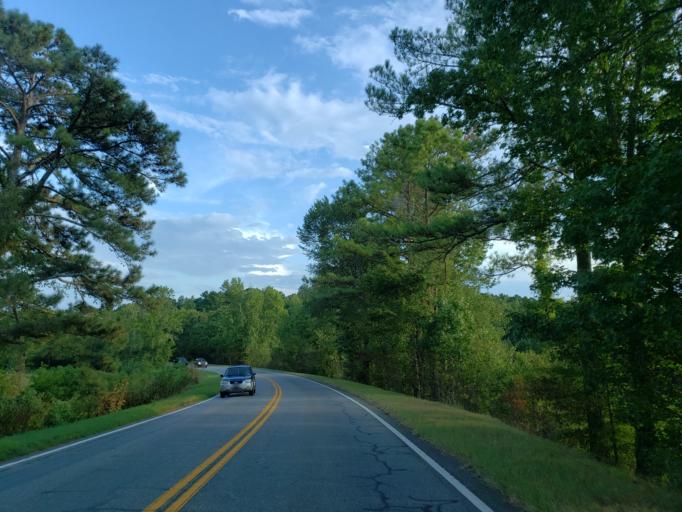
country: US
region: Georgia
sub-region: Bartow County
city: Cartersville
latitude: 34.2216
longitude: -84.8557
